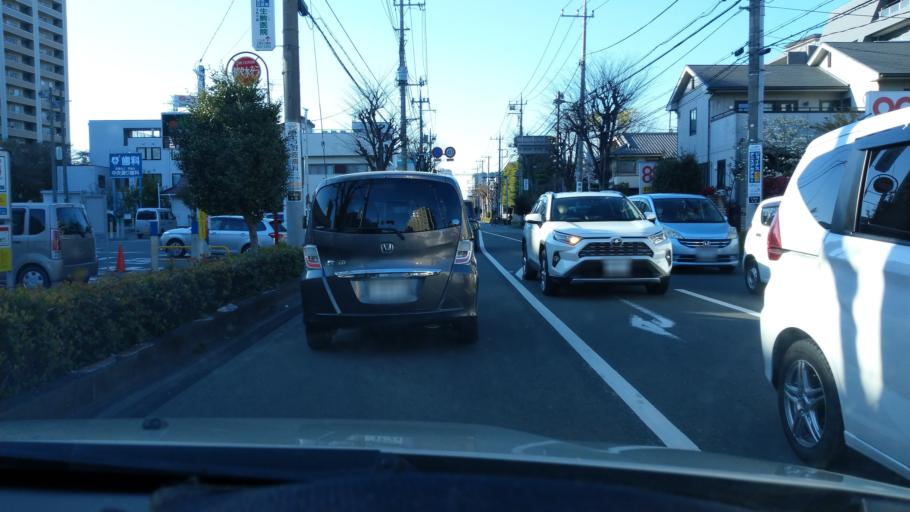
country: JP
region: Saitama
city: Yono
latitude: 35.8918
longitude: 139.6233
